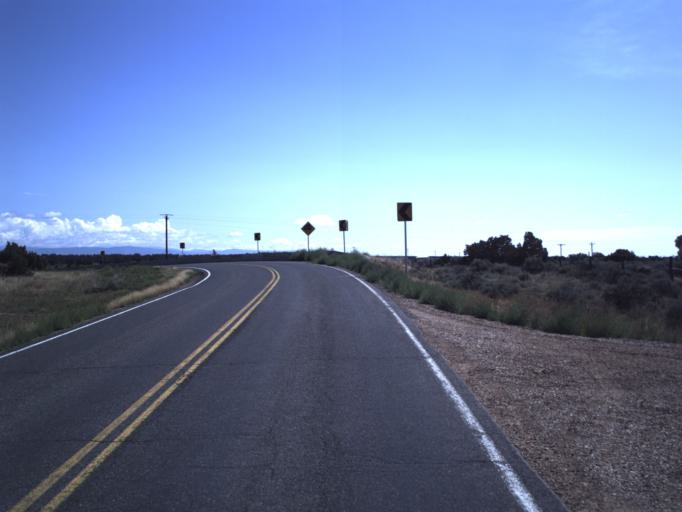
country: US
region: Utah
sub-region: Duchesne County
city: Duchesne
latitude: 40.3526
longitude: -110.3961
